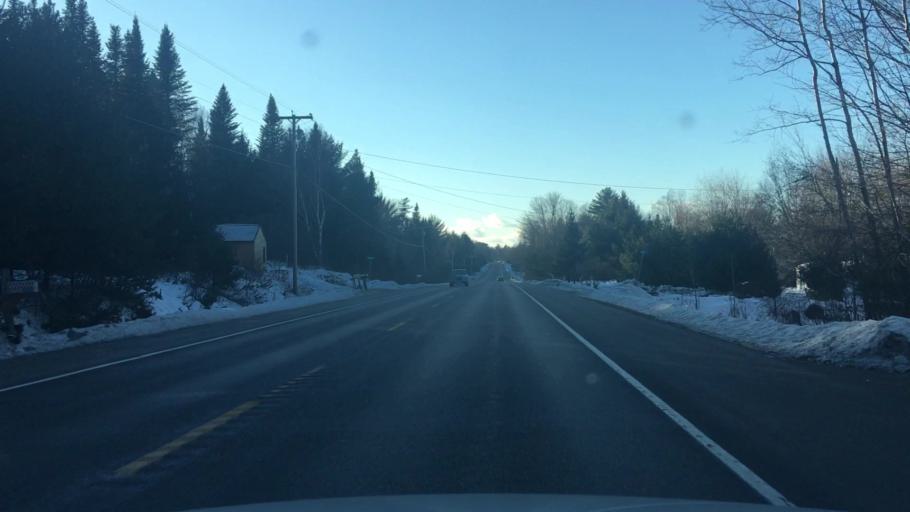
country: US
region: Maine
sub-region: Kennebec County
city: Rome
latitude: 44.6796
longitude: -69.9068
